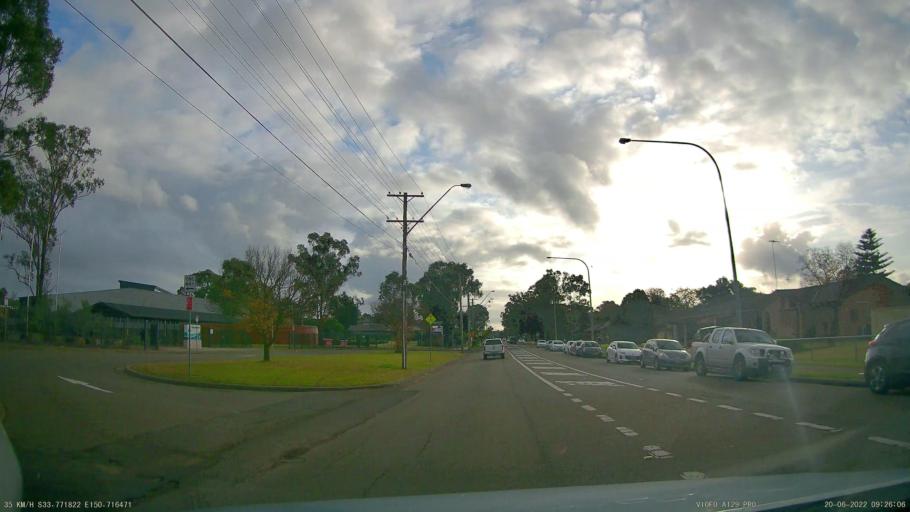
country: AU
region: New South Wales
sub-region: Penrith Municipality
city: Kingswood Park
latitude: -33.7717
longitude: 150.7165
